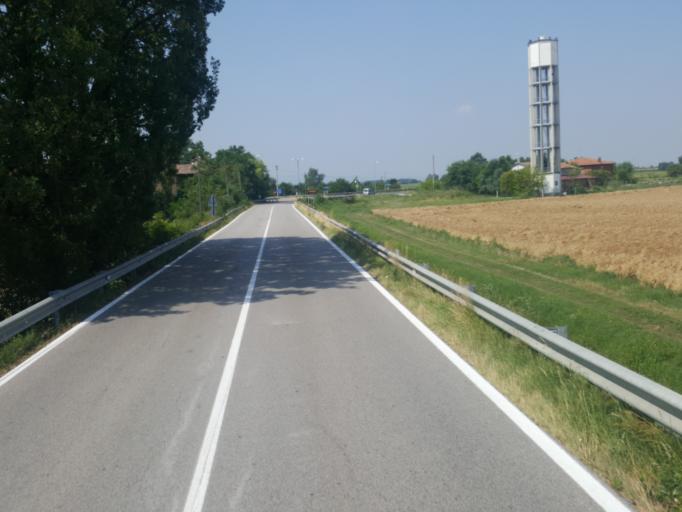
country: IT
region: Emilia-Romagna
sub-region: Provincia di Bologna
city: Sesto Imolese
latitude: 44.4550
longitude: 11.7538
